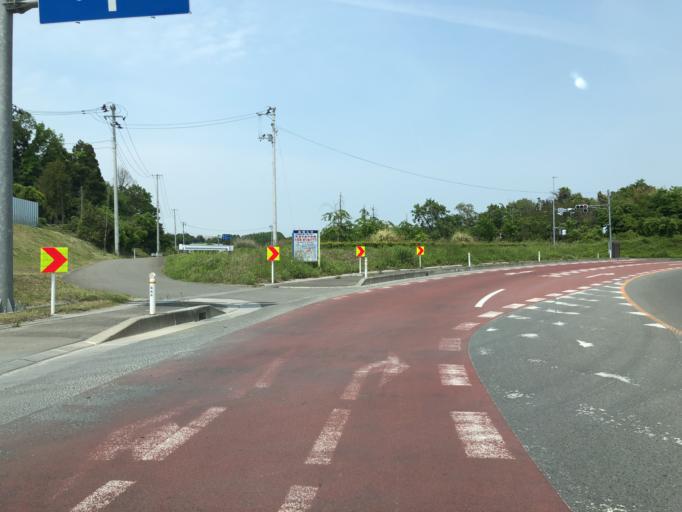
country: JP
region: Miyagi
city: Marumori
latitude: 37.8543
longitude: 140.9200
